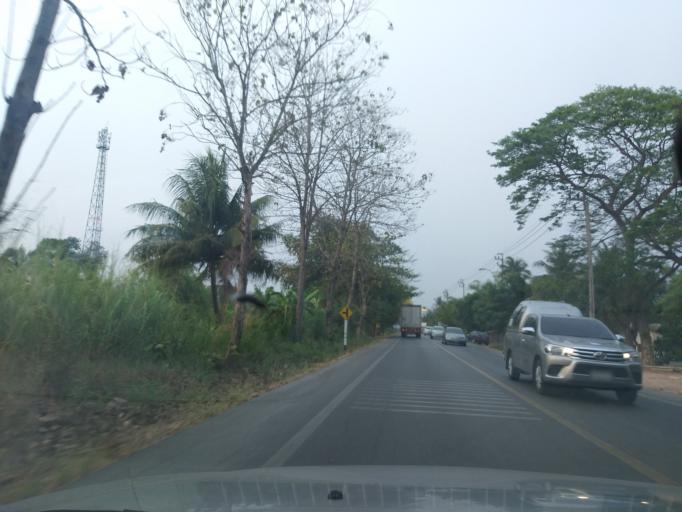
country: TH
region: Bangkok
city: Nong Chok
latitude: 13.8959
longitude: 100.8878
